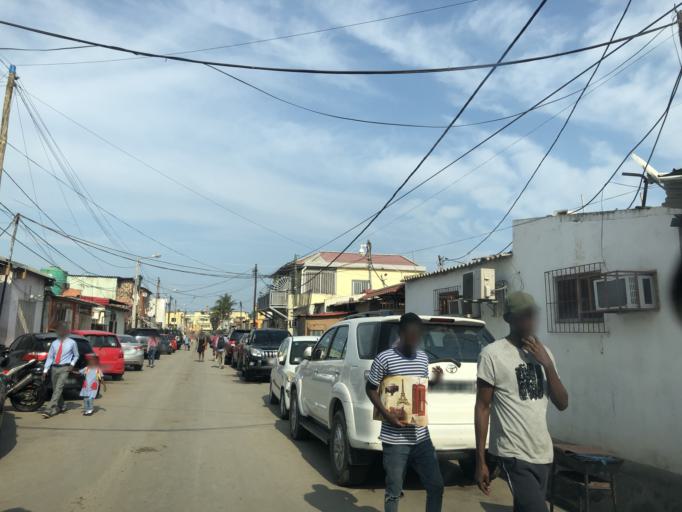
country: AO
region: Luanda
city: Luanda
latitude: -8.8290
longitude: 13.2247
